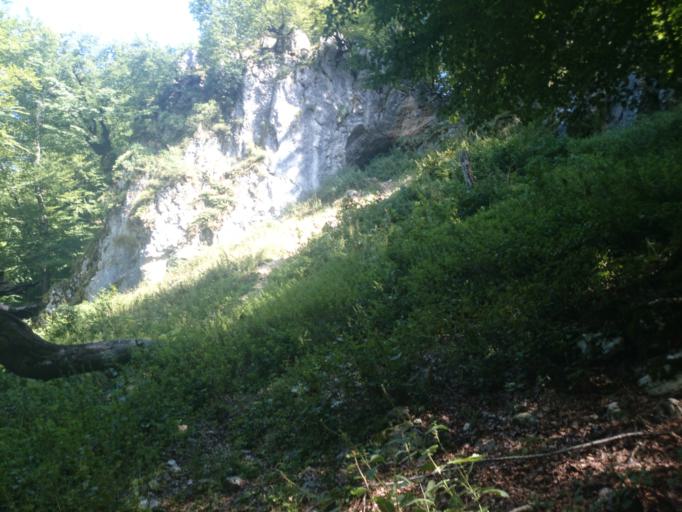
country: AL
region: Elbasan
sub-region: Rrethi i Gramshit
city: Kushove
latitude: 40.7340
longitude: 20.1426
